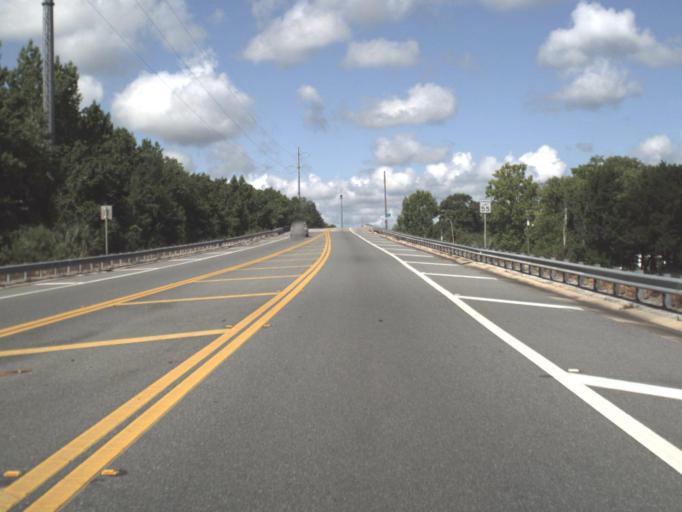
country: US
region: Florida
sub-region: Putnam County
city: Palatka
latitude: 29.5796
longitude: -81.6221
